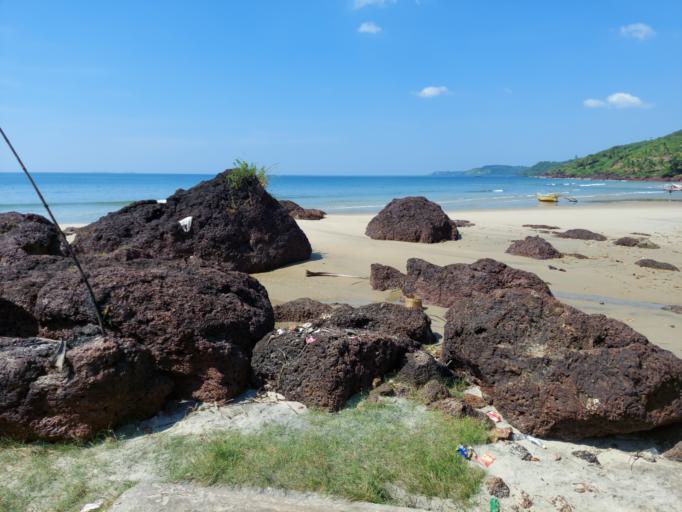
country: IN
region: Maharashtra
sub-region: Sindhudurg
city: Vengurla
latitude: 15.9183
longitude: 73.5677
